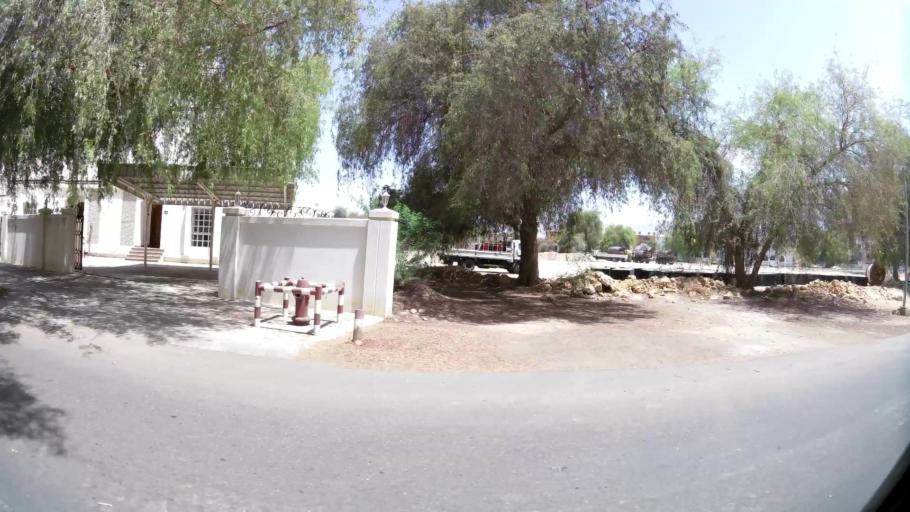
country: OM
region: Muhafazat Masqat
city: Muscat
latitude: 23.6242
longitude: 58.4891
